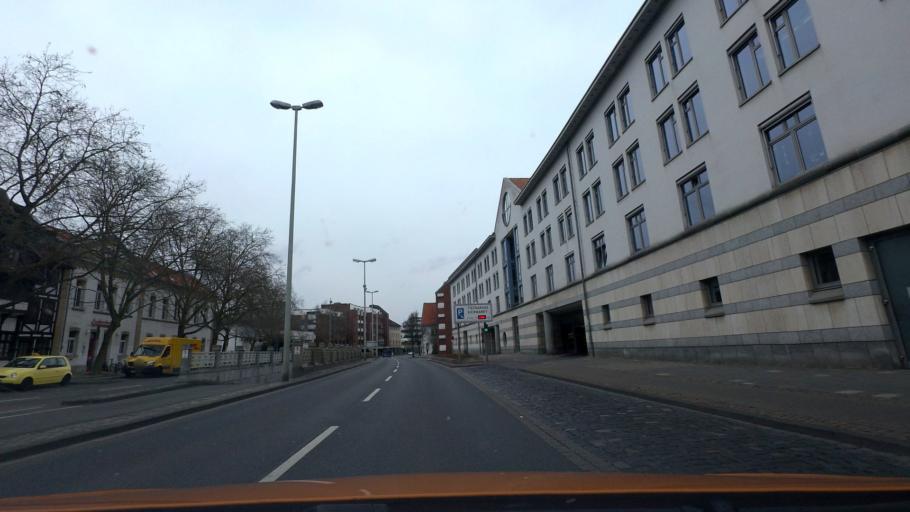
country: DE
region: Lower Saxony
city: Braunschweig
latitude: 52.2608
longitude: 10.5153
